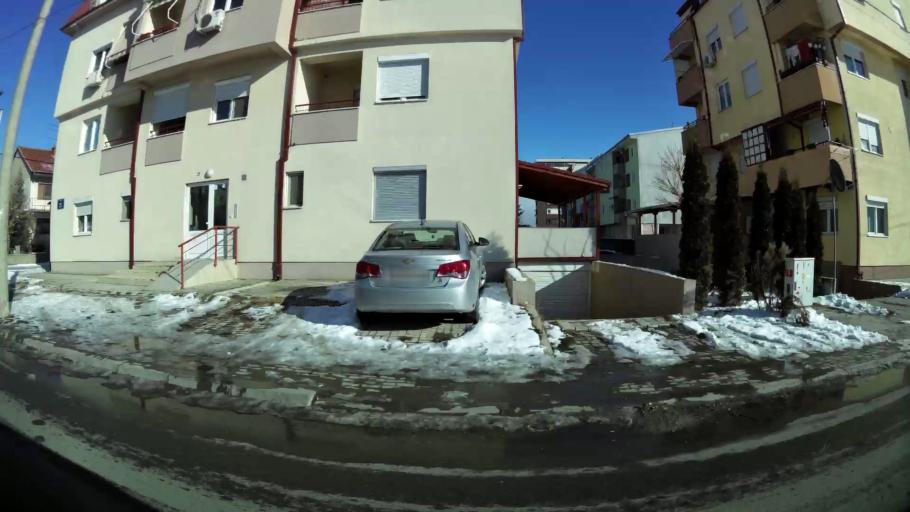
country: MK
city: Krushopek
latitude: 42.0032
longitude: 21.3607
